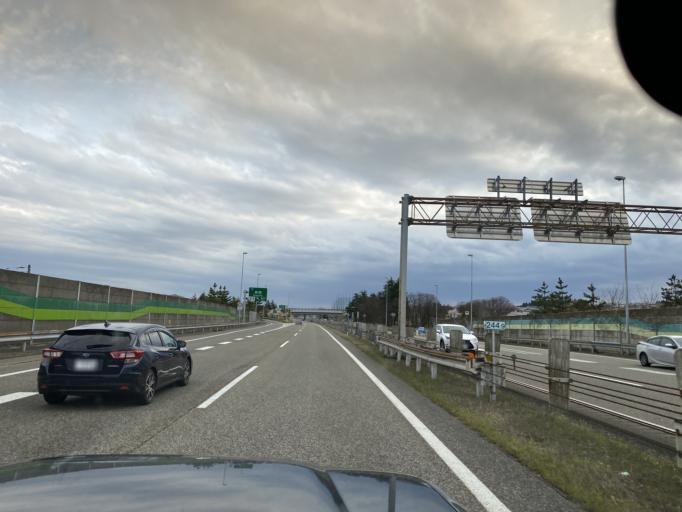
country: JP
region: Niigata
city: Nagaoka
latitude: 37.4491
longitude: 138.7883
